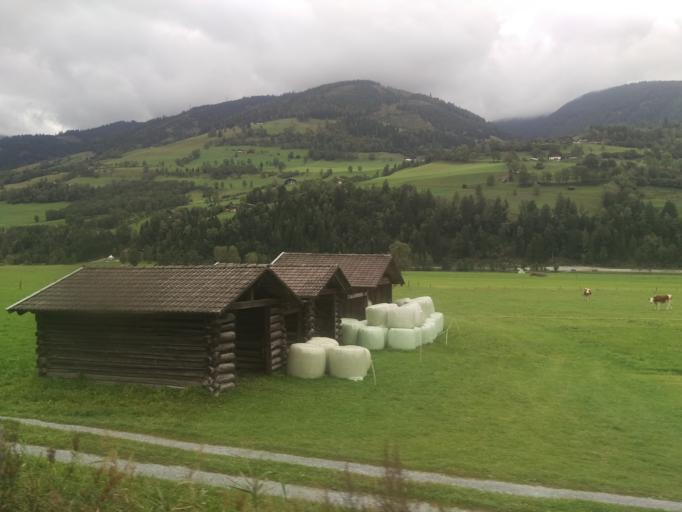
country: AT
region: Salzburg
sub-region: Politischer Bezirk Zell am See
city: Niedernsill
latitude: 47.2808
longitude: 12.6125
